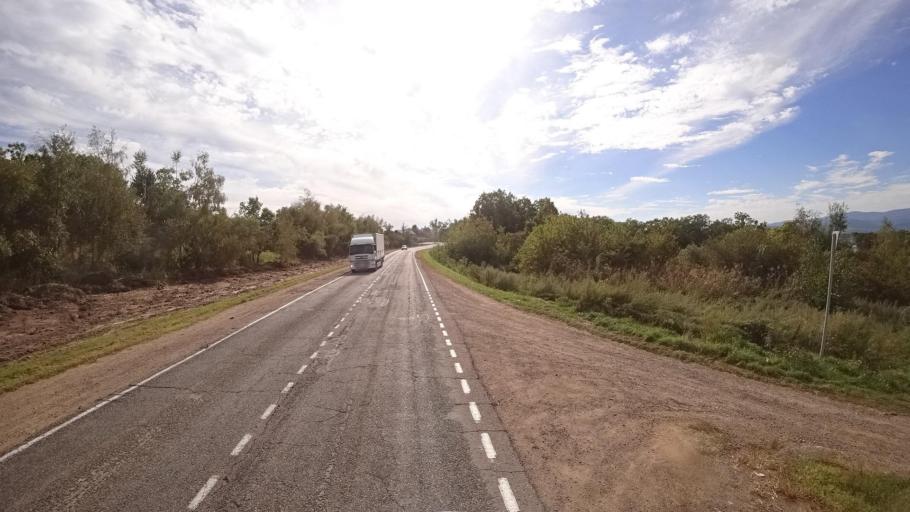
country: RU
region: Primorskiy
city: Dostoyevka
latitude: 44.3232
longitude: 133.4868
